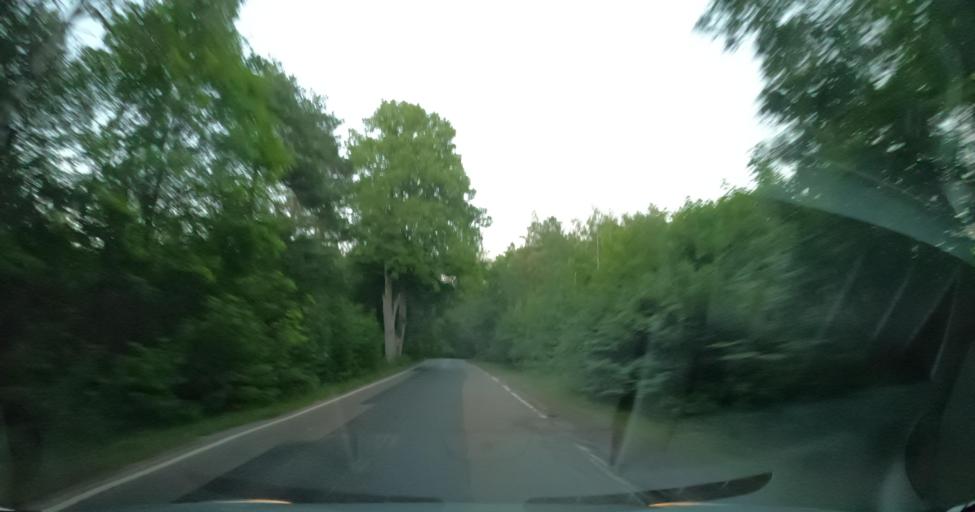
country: PL
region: Pomeranian Voivodeship
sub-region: Powiat wejherowski
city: Luzino
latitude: 54.4658
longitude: 18.1133
